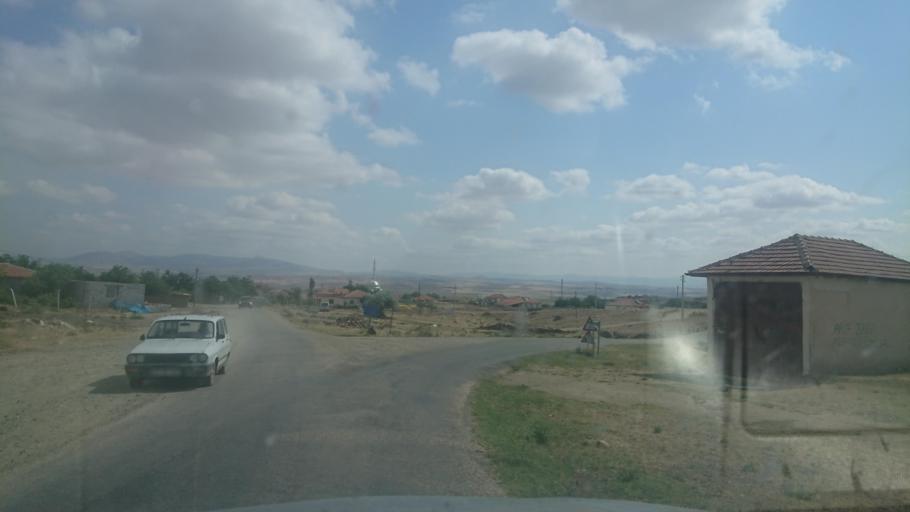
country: TR
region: Aksaray
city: Sariyahsi
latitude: 39.0112
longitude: 33.9443
